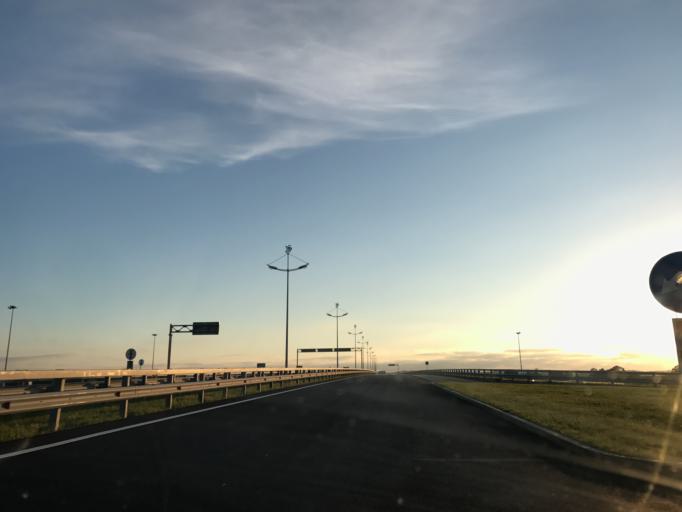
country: RU
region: Kaliningrad
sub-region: Gorod Kaliningrad
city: Pionerskiy
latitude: 54.9215
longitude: 20.3314
